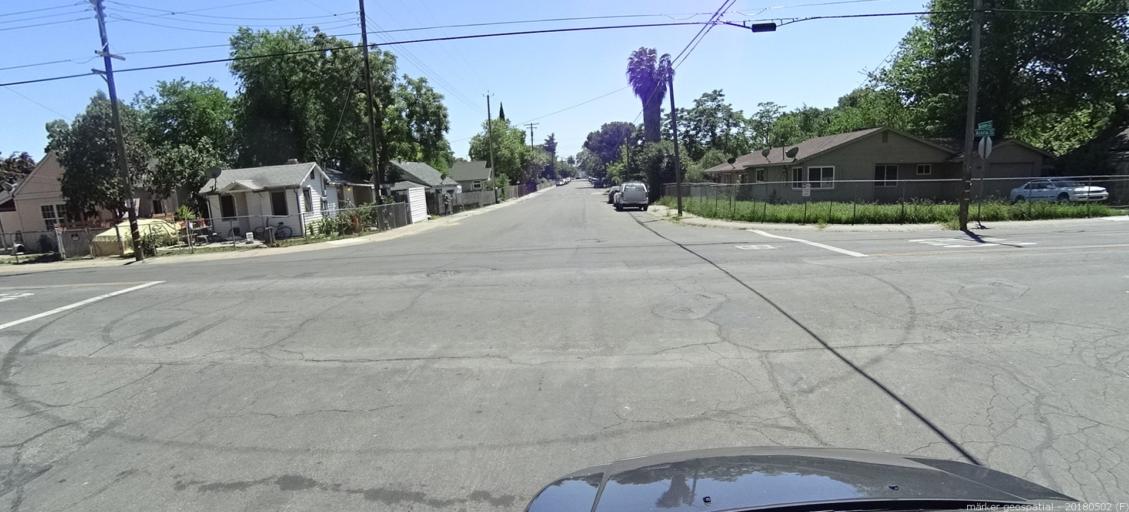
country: US
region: California
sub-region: Sacramento County
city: Arden-Arcade
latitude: 38.6221
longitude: -121.4416
